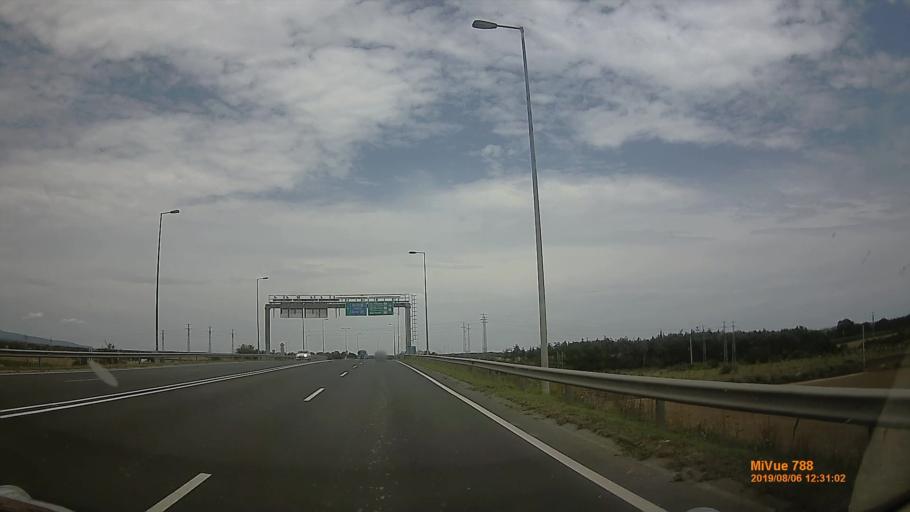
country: HU
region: Vas
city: Szombathely
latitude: 47.2451
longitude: 16.6544
